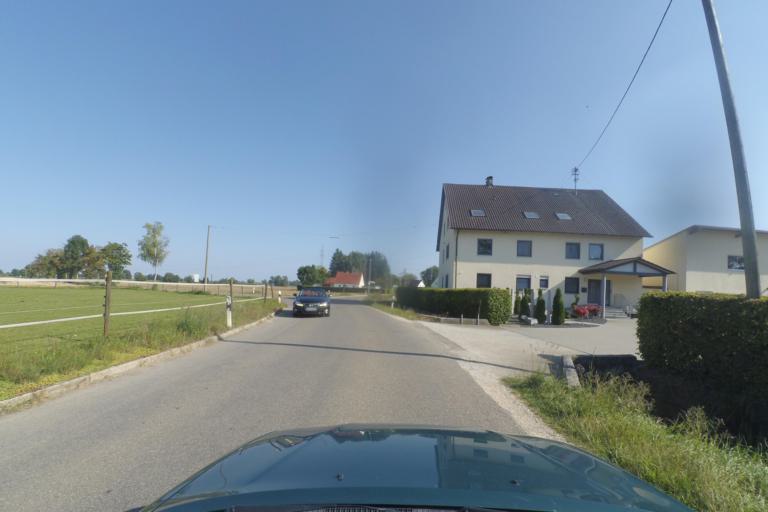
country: DE
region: Bavaria
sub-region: Swabia
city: Tapfheim
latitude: 48.6653
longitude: 10.7229
